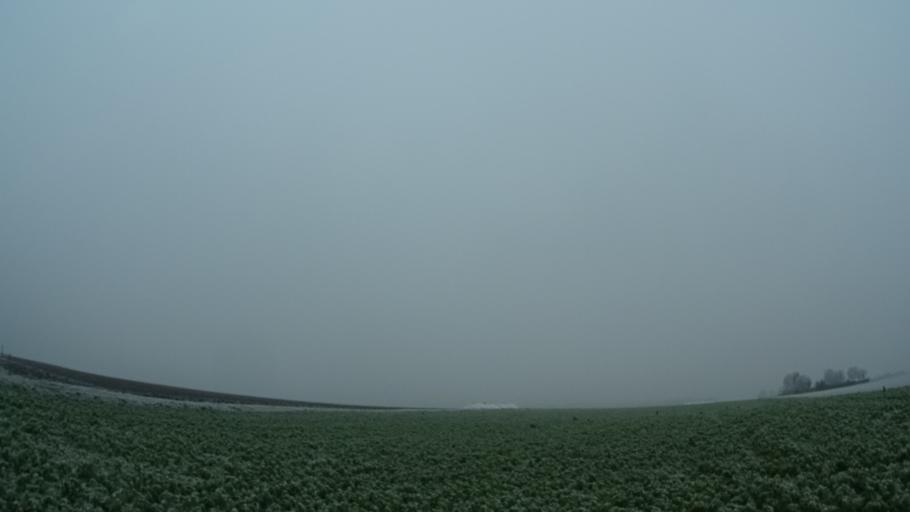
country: DE
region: Bavaria
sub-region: Regierungsbezirk Unterfranken
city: Lulsfeld
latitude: 49.8421
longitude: 10.2988
